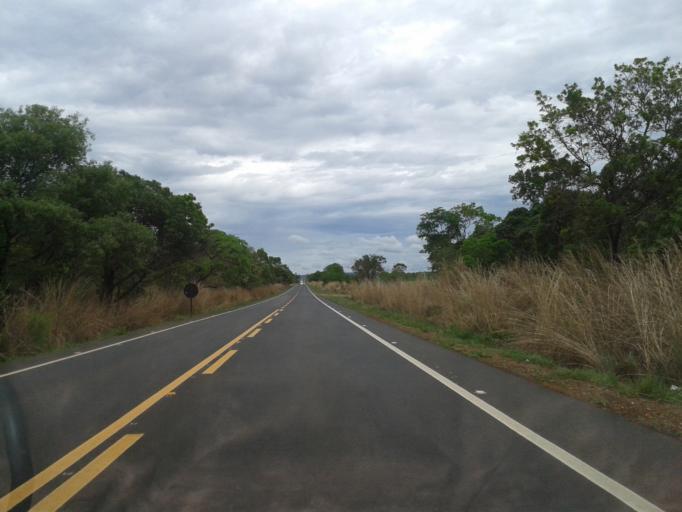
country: BR
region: Goias
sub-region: Caldas Novas
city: Caldas Novas
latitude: -17.8621
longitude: -48.6415
